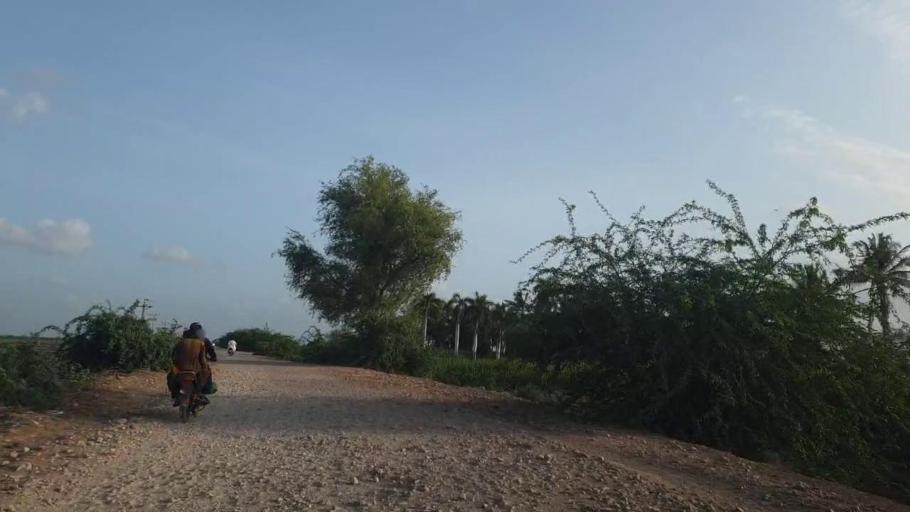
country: PK
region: Sindh
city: Kadhan
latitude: 24.6304
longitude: 69.1158
